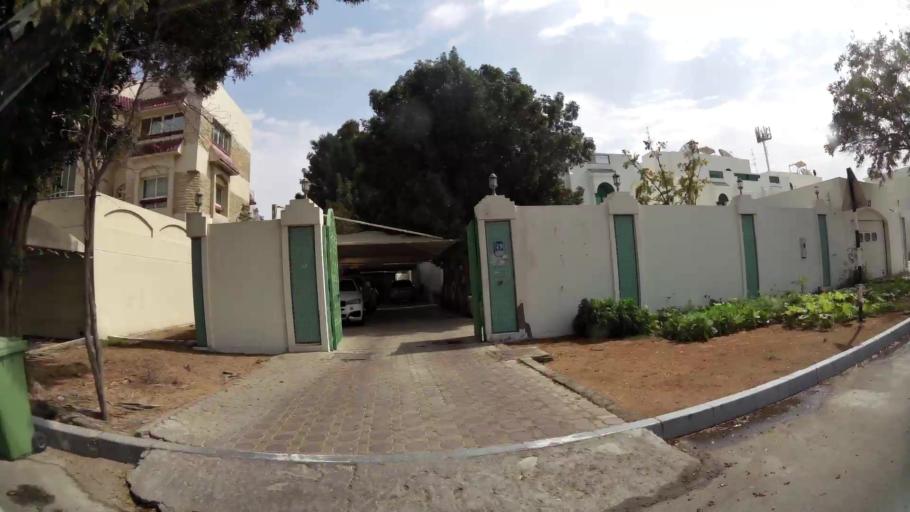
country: AE
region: Abu Dhabi
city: Abu Dhabi
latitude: 24.4148
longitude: 54.4711
